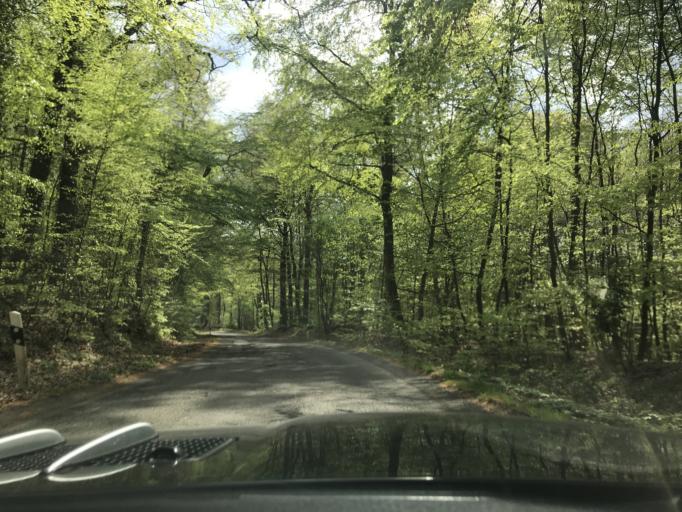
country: DE
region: Schleswig-Holstein
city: Ratekau
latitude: 53.9155
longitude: 10.7860
